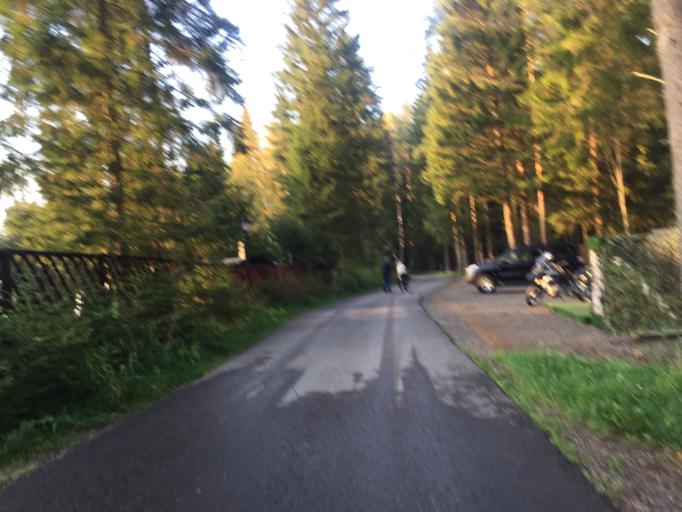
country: RU
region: Leningrad
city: Toksovo
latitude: 60.1281
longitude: 30.4530
